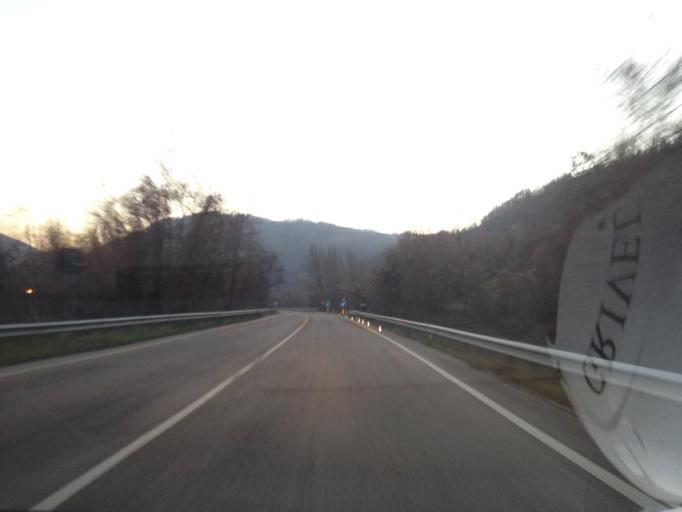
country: IT
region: The Marches
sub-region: Provincia di Ascoli Piceno
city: Arquata del Tronto
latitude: 42.7426
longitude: 13.2657
